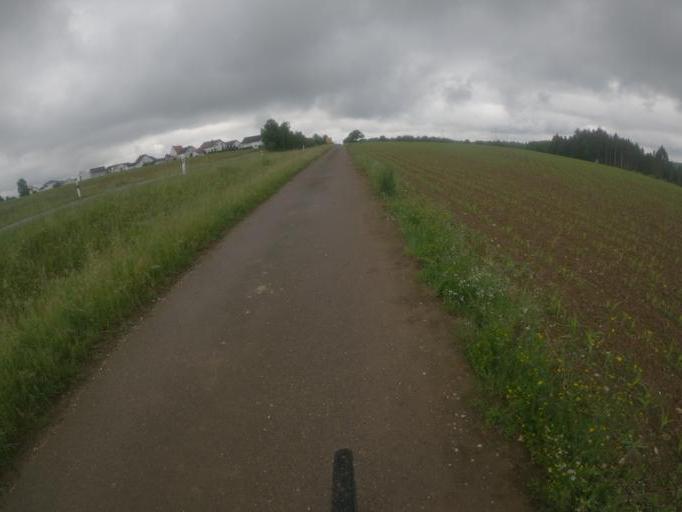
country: DE
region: Baden-Wuerttemberg
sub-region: Regierungsbezirk Stuttgart
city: Adelberg
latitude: 48.7670
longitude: 9.5925
